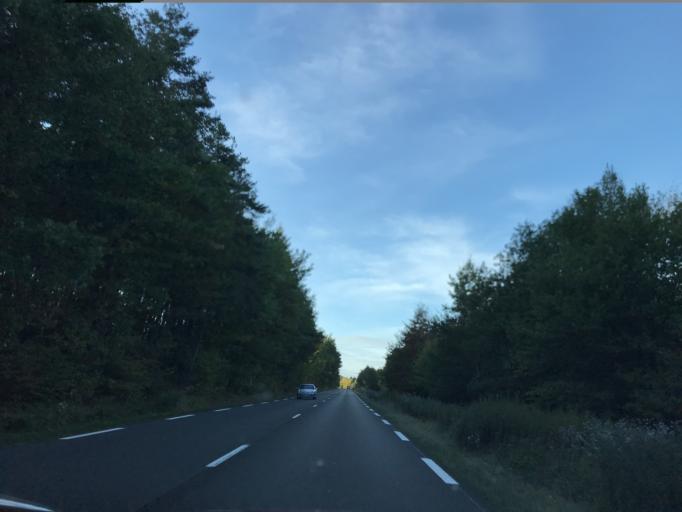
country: FR
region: Auvergne
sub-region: Departement du Puy-de-Dome
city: Paslieres
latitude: 45.9171
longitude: 3.5117
